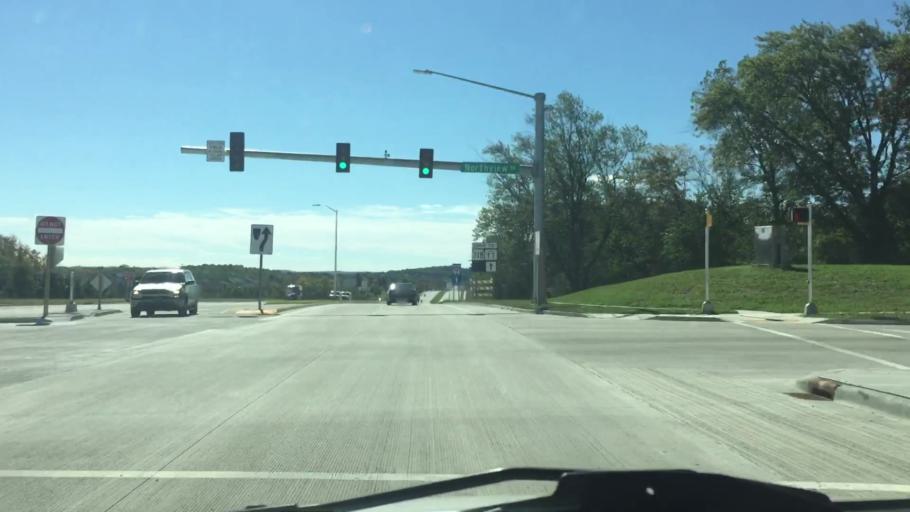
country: US
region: Wisconsin
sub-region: Waukesha County
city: Pewaukee
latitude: 43.0366
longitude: -88.2859
